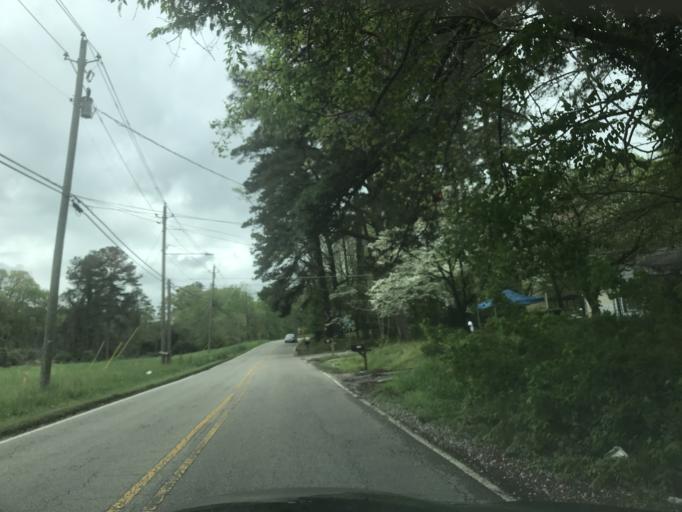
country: US
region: North Carolina
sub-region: Wake County
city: Raleigh
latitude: 35.7472
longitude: -78.6527
